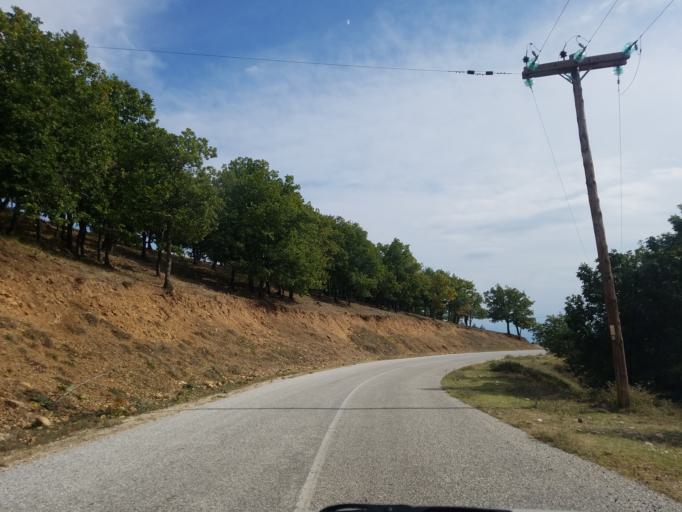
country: GR
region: Thessaly
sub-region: Trikala
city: Kastraki
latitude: 39.7665
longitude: 21.6664
